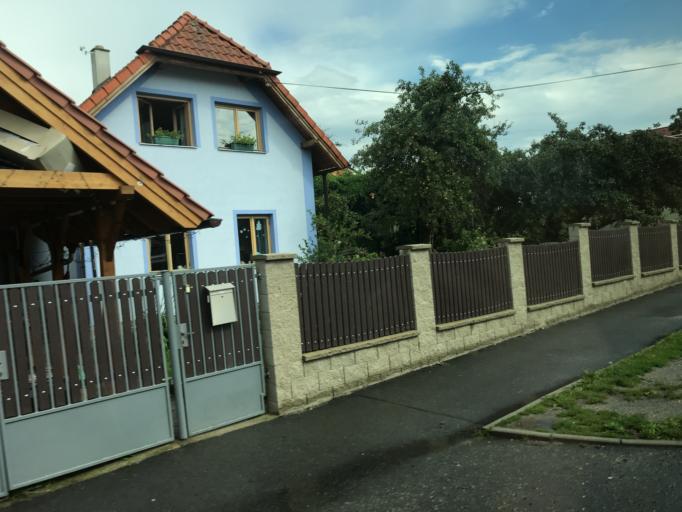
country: CZ
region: Jihocesky
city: Vcelna
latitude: 48.9226
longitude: 14.4535
